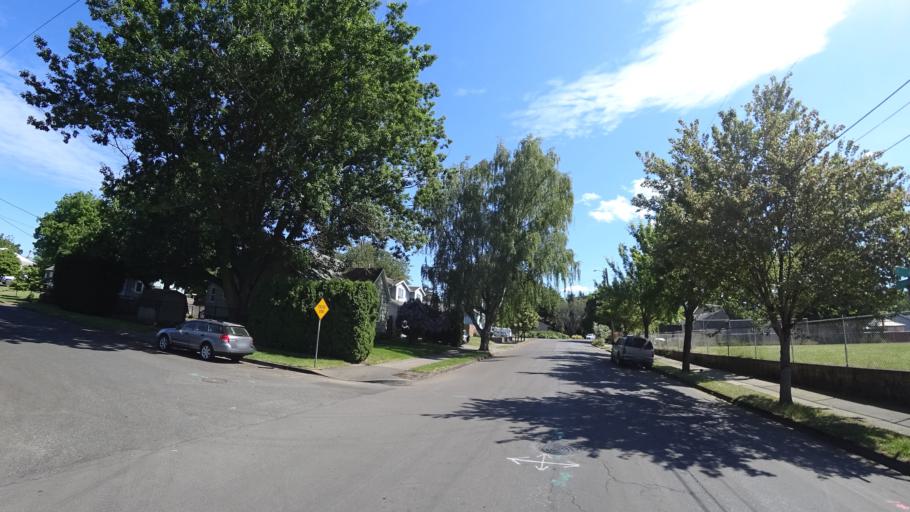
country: US
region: Oregon
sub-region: Washington County
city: West Haven
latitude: 45.5953
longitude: -122.7348
